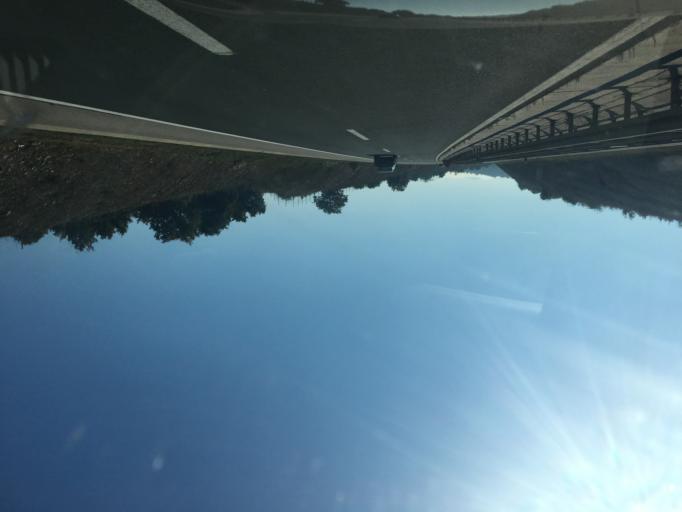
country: HR
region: Licko-Senjska
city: Gospic
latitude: 44.6589
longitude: 15.4264
